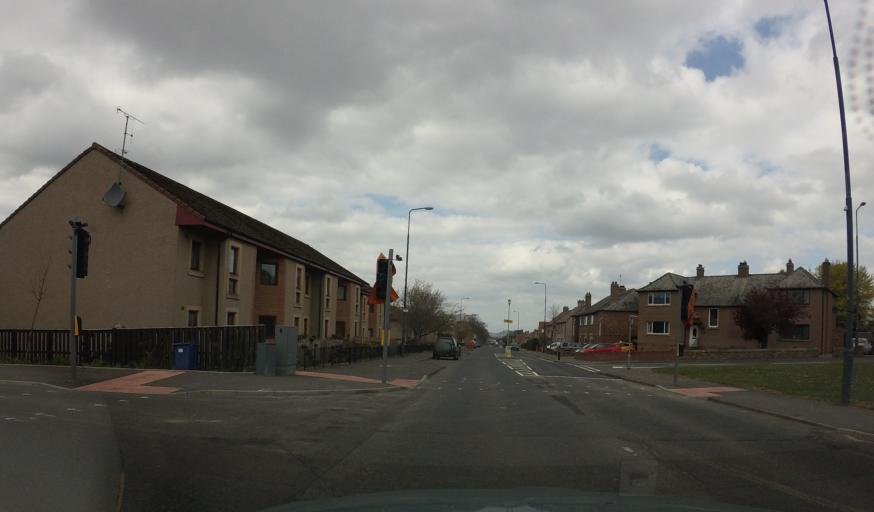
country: GB
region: Scotland
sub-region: Midlothian
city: Gorebridge
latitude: 55.8492
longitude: -3.0558
